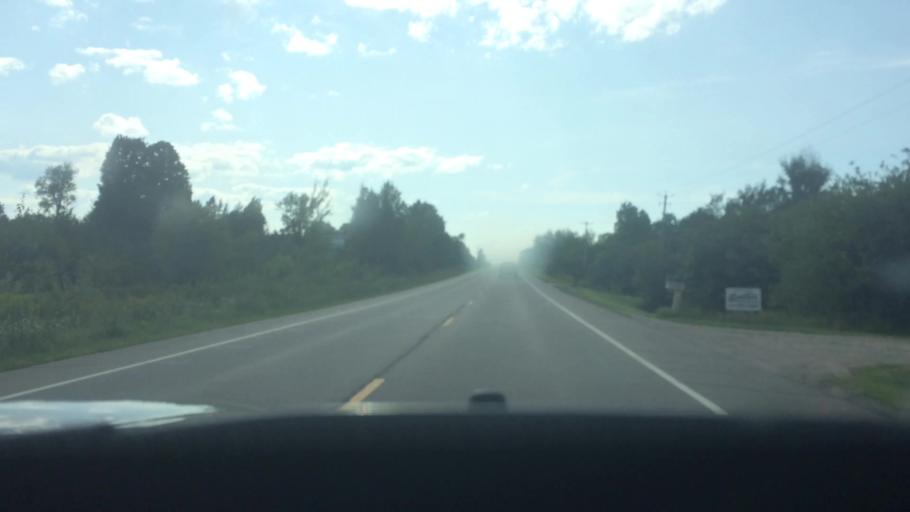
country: US
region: New York
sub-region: Franklin County
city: Malone
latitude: 44.8455
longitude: -74.1738
